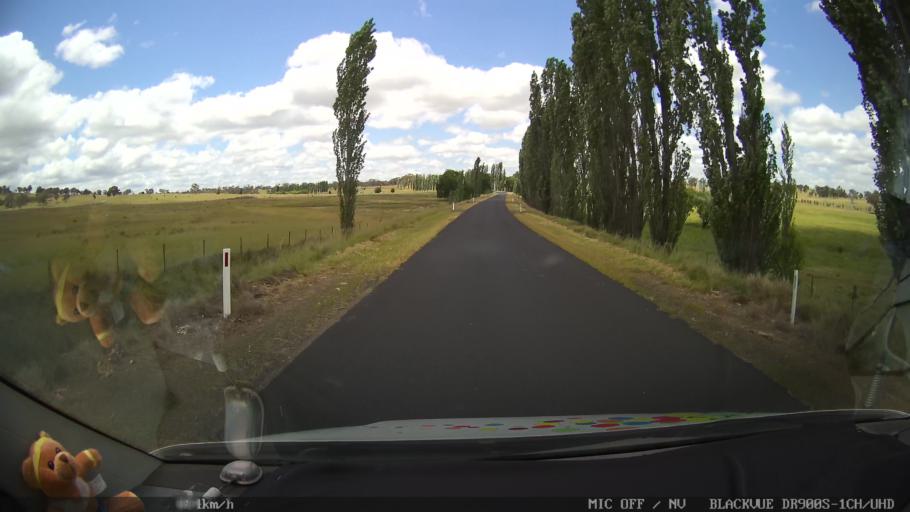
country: AU
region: New South Wales
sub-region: Glen Innes Severn
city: Glen Innes
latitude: -29.4333
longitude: 151.7543
